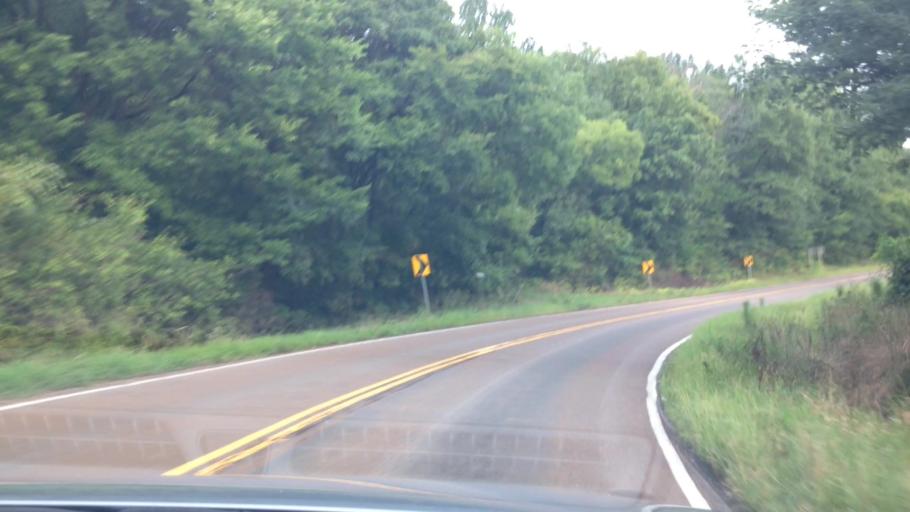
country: US
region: Missouri
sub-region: Clay County
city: Smithville
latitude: 39.4066
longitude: -94.6580
